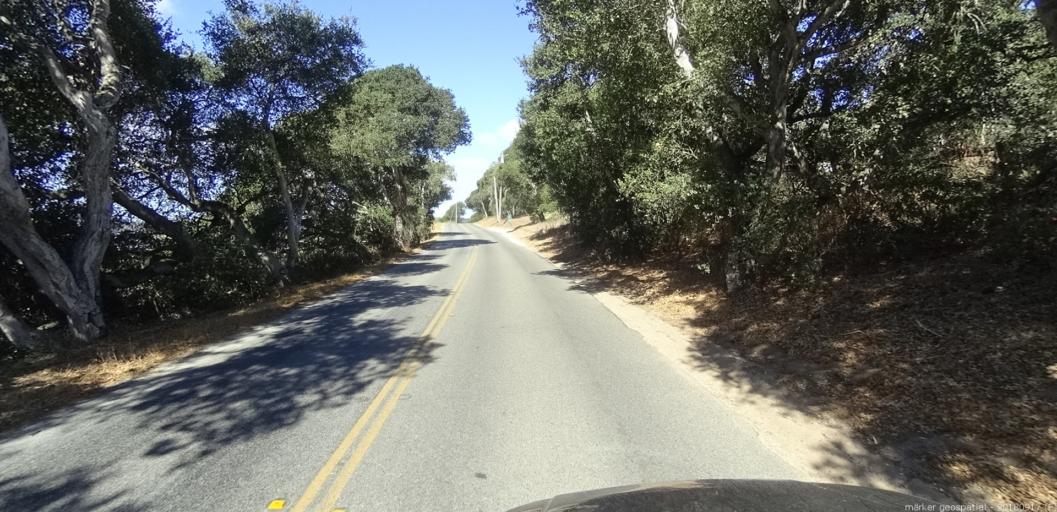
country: US
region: California
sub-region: Monterey County
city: Elkhorn
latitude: 36.8397
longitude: -121.7347
